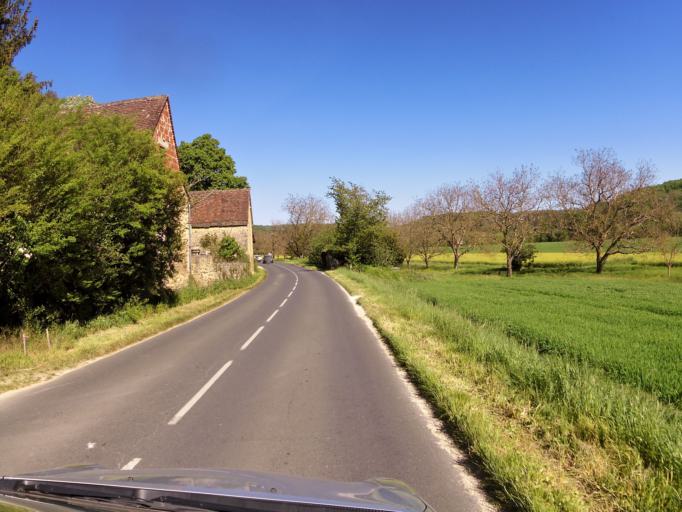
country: FR
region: Aquitaine
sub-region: Departement de la Dordogne
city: Cenac-et-Saint-Julien
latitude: 44.8218
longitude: 1.1608
